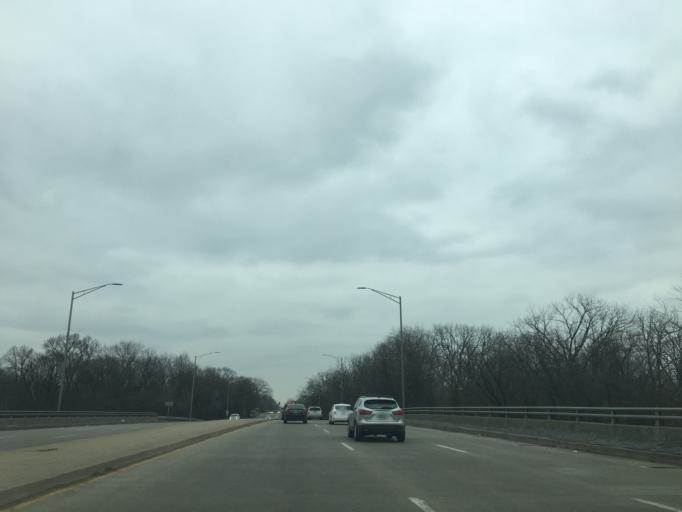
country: US
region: Illinois
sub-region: Cook County
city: North Riverside
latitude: 41.8499
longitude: -87.8280
